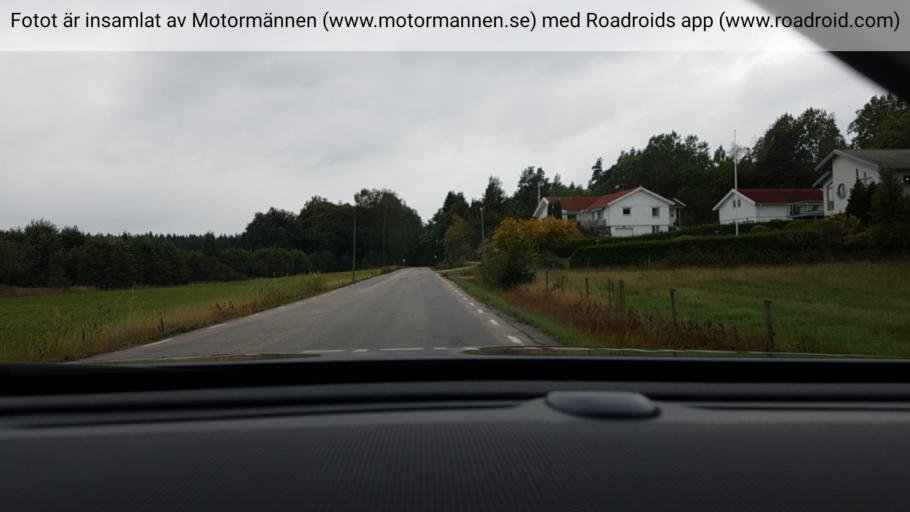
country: SE
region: Vaestra Goetaland
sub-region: Vanersborgs Kommun
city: Vanersborg
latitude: 58.3602
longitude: 12.2664
